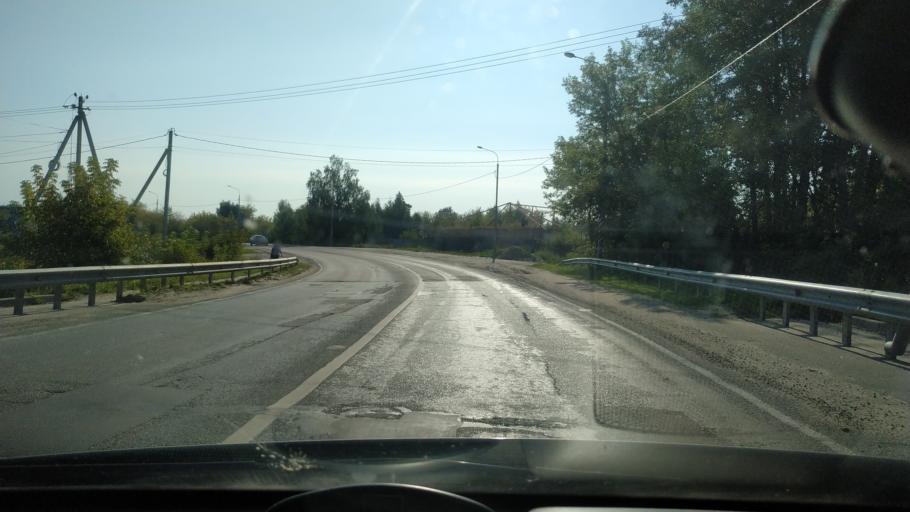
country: RU
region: Moskovskaya
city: Kerva
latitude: 55.5608
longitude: 39.6774
